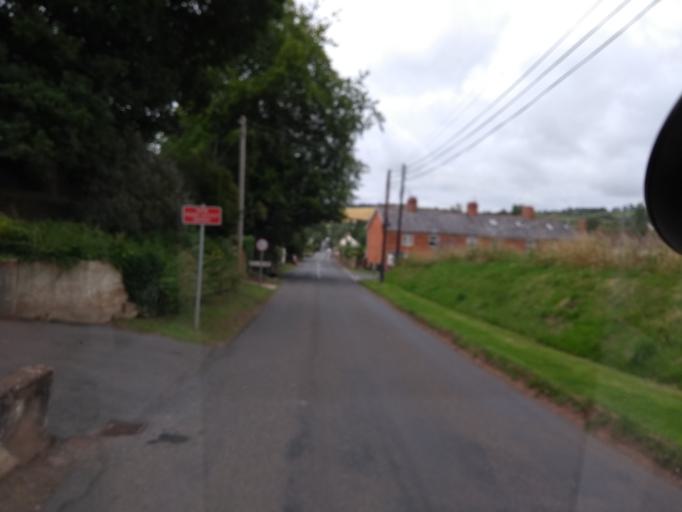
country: GB
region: England
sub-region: Somerset
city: Wiveliscombe
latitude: 51.0451
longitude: -3.3058
